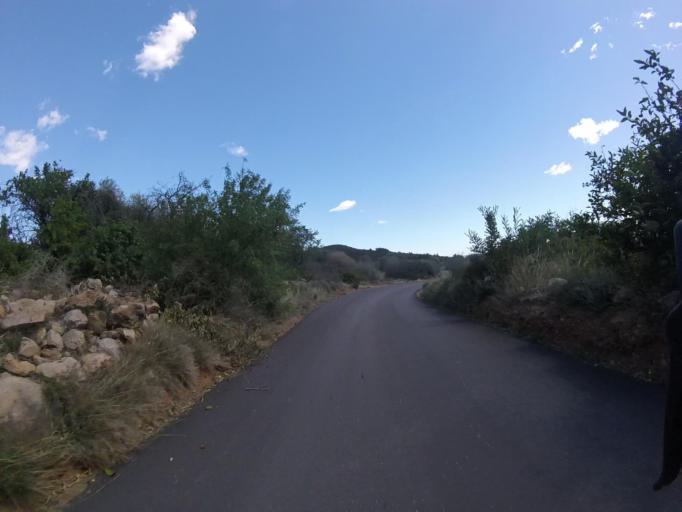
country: ES
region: Valencia
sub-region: Provincia de Castello
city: Orpesa/Oropesa del Mar
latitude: 40.1682
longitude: 0.1443
